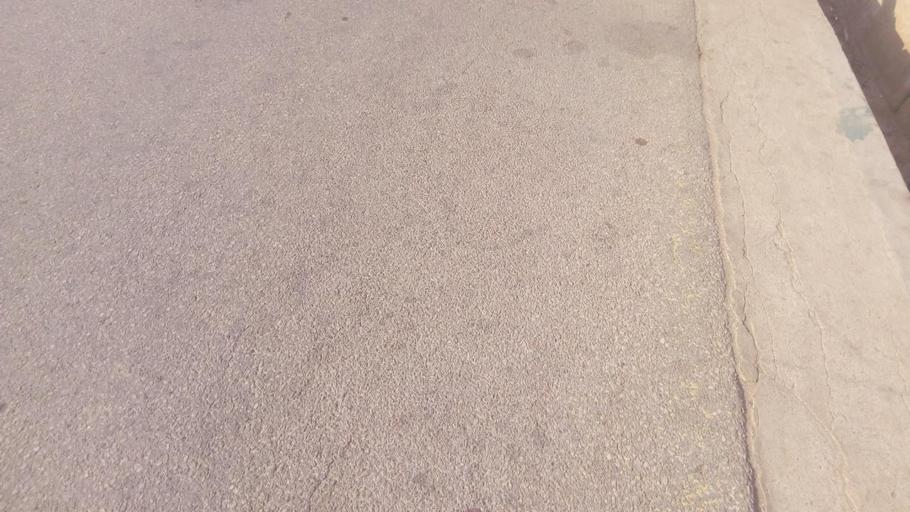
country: ZM
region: Lusaka
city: Lusaka
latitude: -15.3623
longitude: 28.3039
